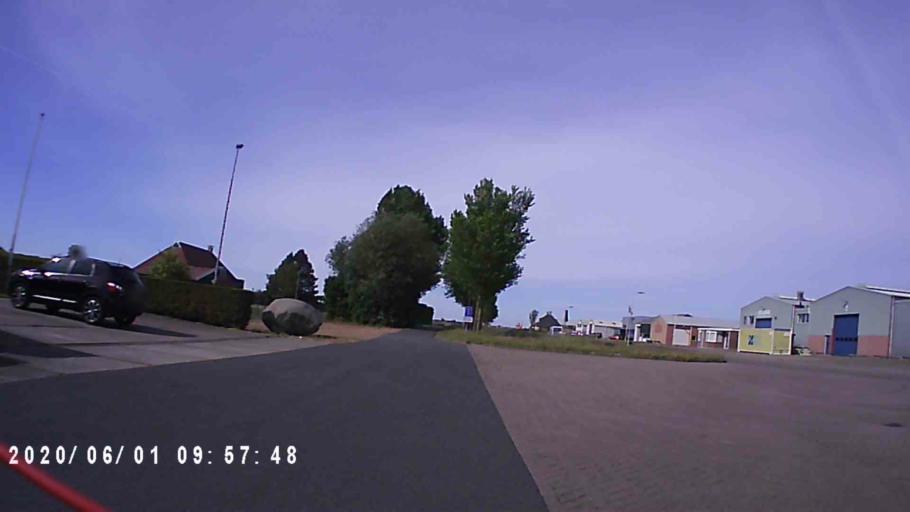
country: NL
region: Friesland
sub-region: Menameradiel
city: Berltsum
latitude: 53.2381
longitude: 5.6442
